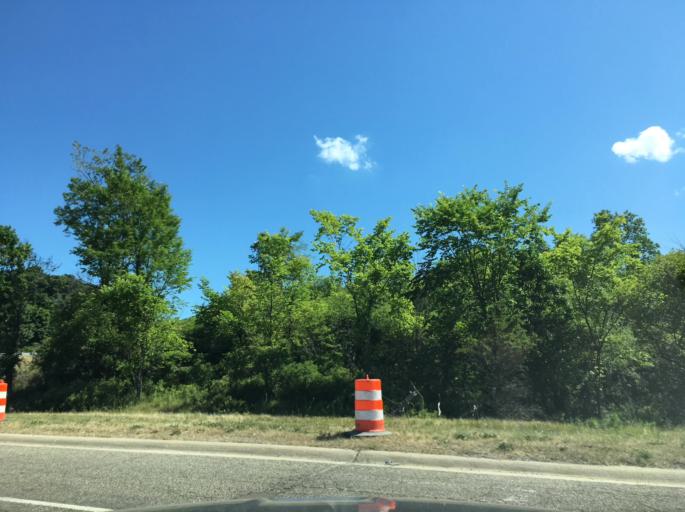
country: US
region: Michigan
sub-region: Oakland County
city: Auburn Hills
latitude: 42.6965
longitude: -83.2796
